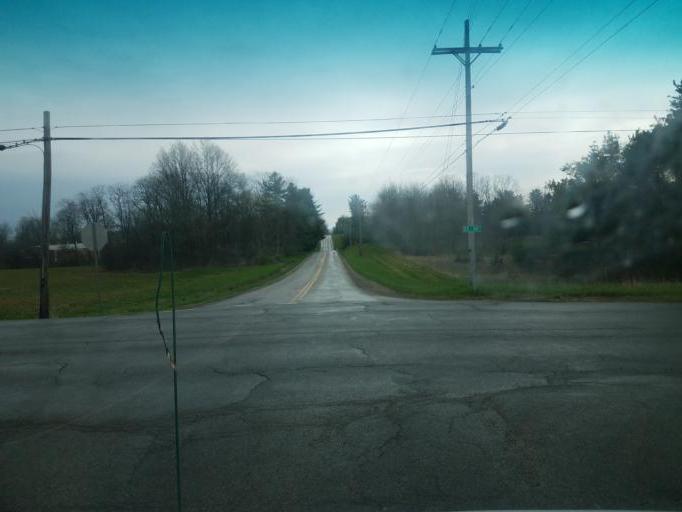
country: US
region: Ohio
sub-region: Ashland County
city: Ashland
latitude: 40.8286
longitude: -82.2990
